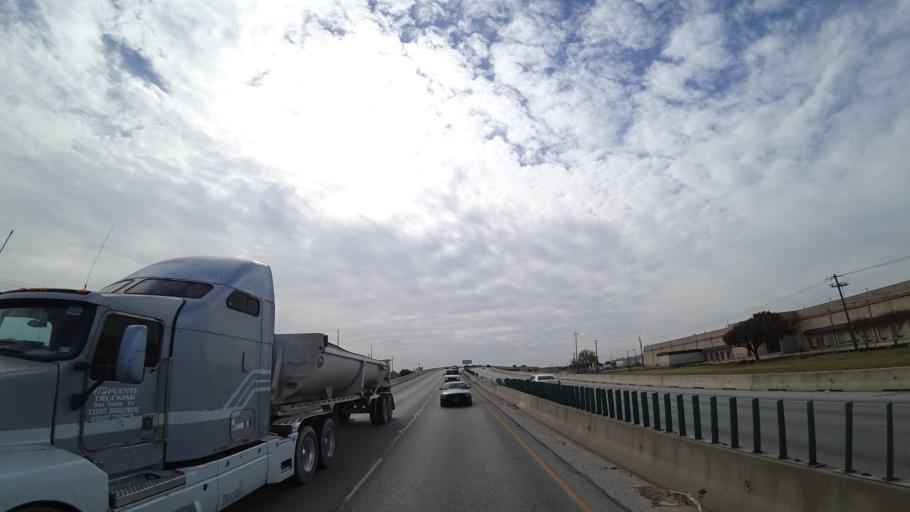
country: US
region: Texas
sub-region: Travis County
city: Austin
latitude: 30.2564
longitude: -97.6769
